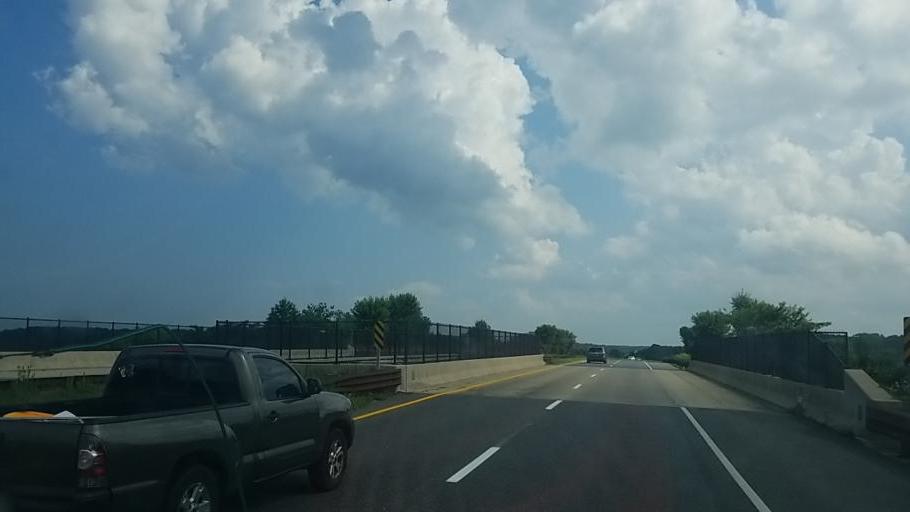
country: US
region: Maryland
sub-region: Worcester County
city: Ocean Pines
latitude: 38.3911
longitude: -75.2037
